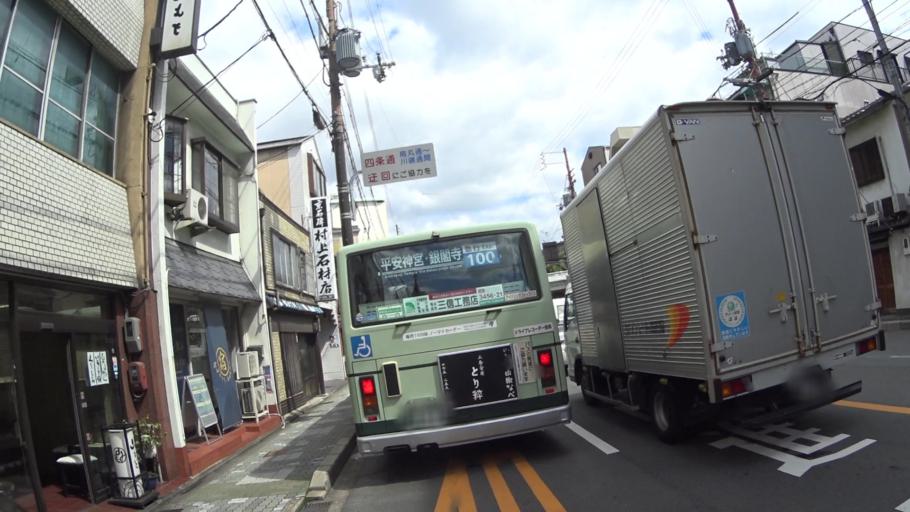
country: JP
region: Kyoto
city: Kyoto
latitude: 34.9931
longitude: 135.7751
